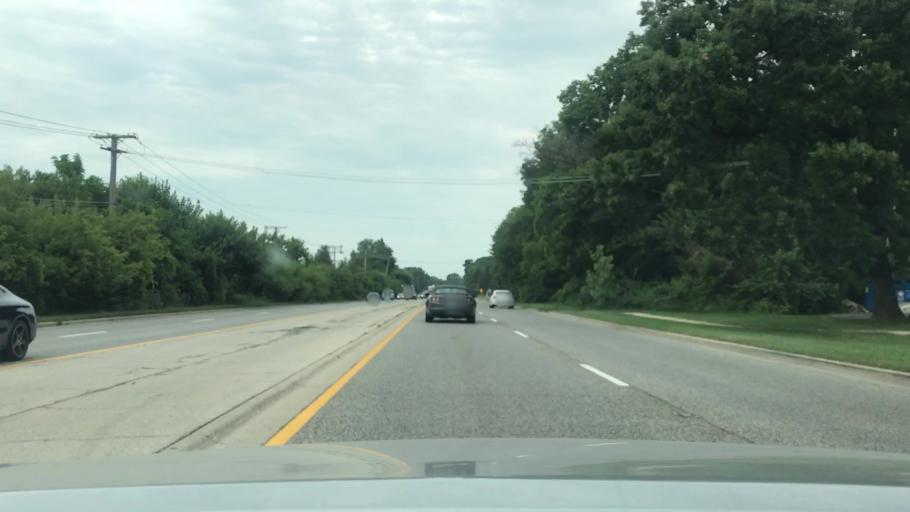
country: US
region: Illinois
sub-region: DuPage County
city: Woodridge
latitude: 41.7379
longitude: -88.0628
